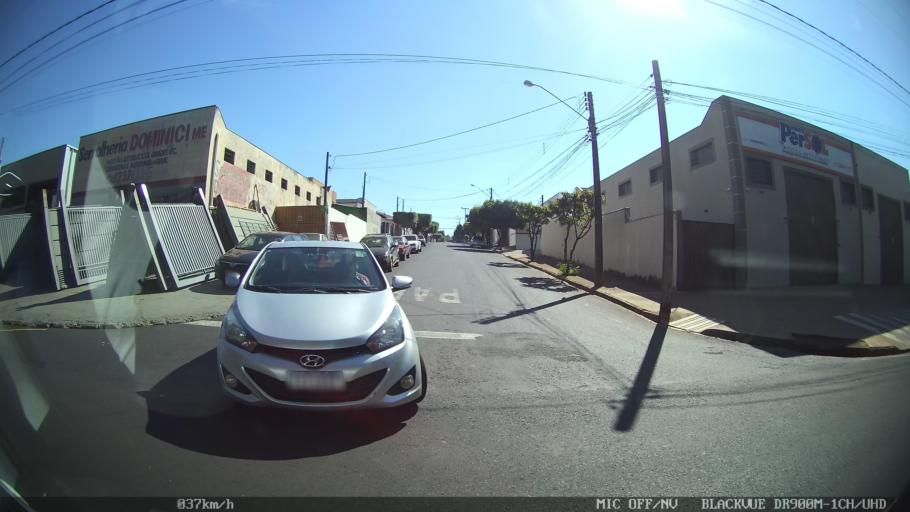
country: BR
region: Sao Paulo
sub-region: Sao Jose Do Rio Preto
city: Sao Jose do Rio Preto
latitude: -20.8032
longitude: -49.4164
